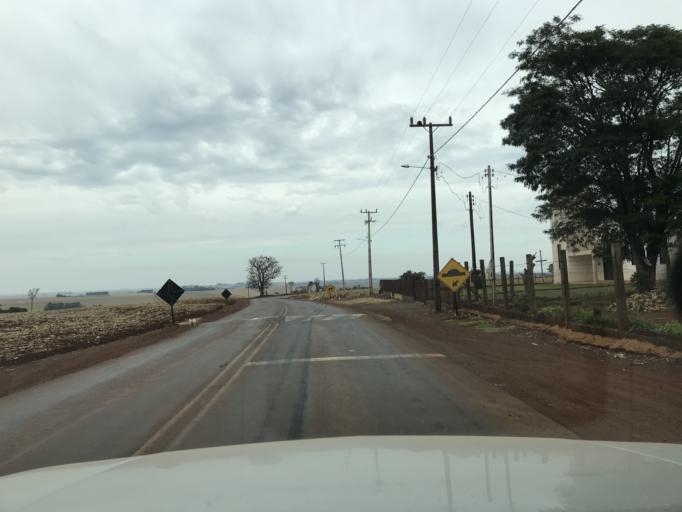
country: BR
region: Parana
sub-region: Palotina
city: Palotina
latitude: -24.4194
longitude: -53.8824
